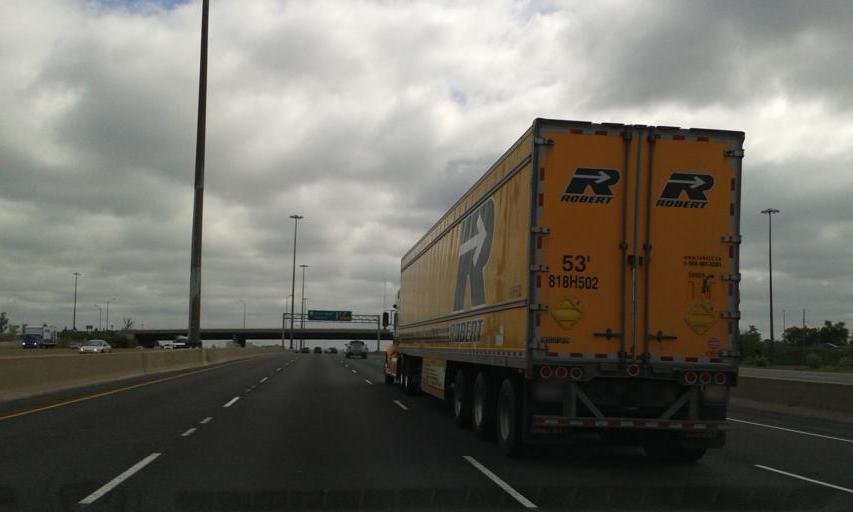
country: CA
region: Ontario
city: Pickering
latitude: 43.8079
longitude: -79.1282
